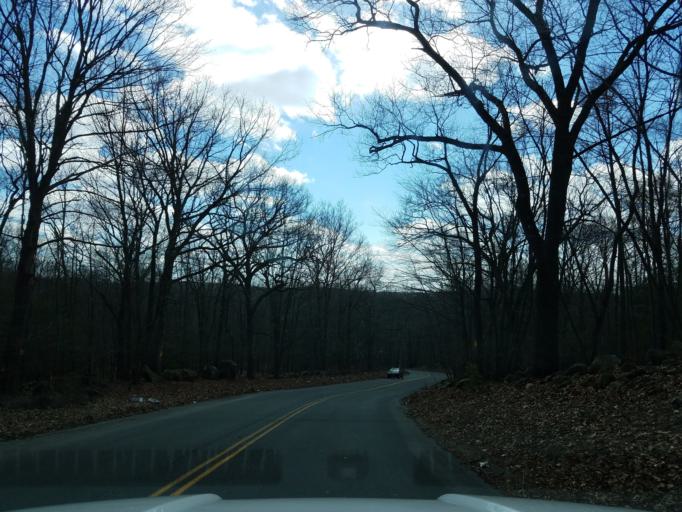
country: US
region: Connecticut
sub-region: New Haven County
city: Naugatuck
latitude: 41.4772
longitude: -73.0191
